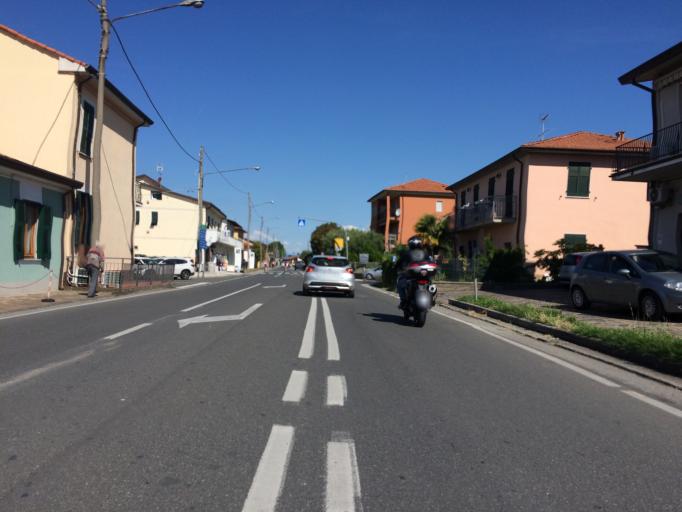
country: IT
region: Liguria
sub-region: Provincia di La Spezia
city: Casano-Dogana-Isola
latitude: 44.0705
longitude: 10.0243
